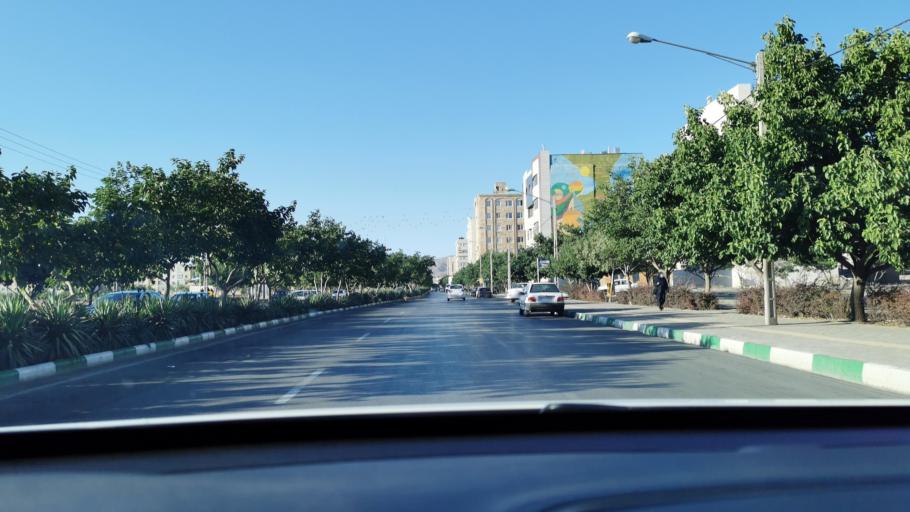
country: IR
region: Razavi Khorasan
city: Mashhad
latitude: 36.3551
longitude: 59.4880
